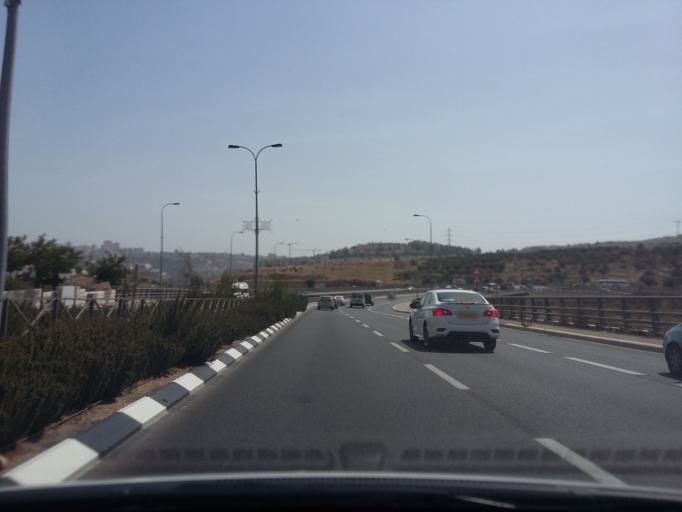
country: PS
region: West Bank
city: Bir Nabala
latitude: 31.8269
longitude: 35.2170
